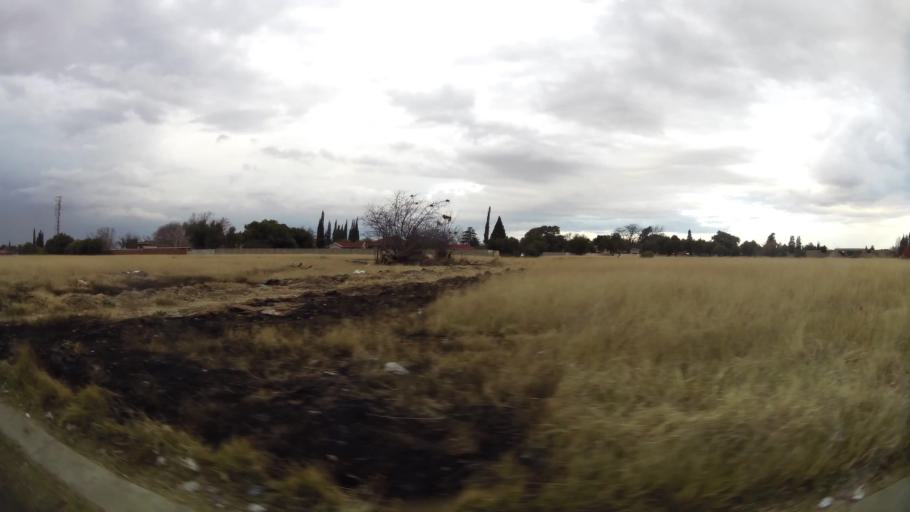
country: ZA
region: Orange Free State
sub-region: Lejweleputswa District Municipality
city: Welkom
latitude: -27.9566
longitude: 26.7236
